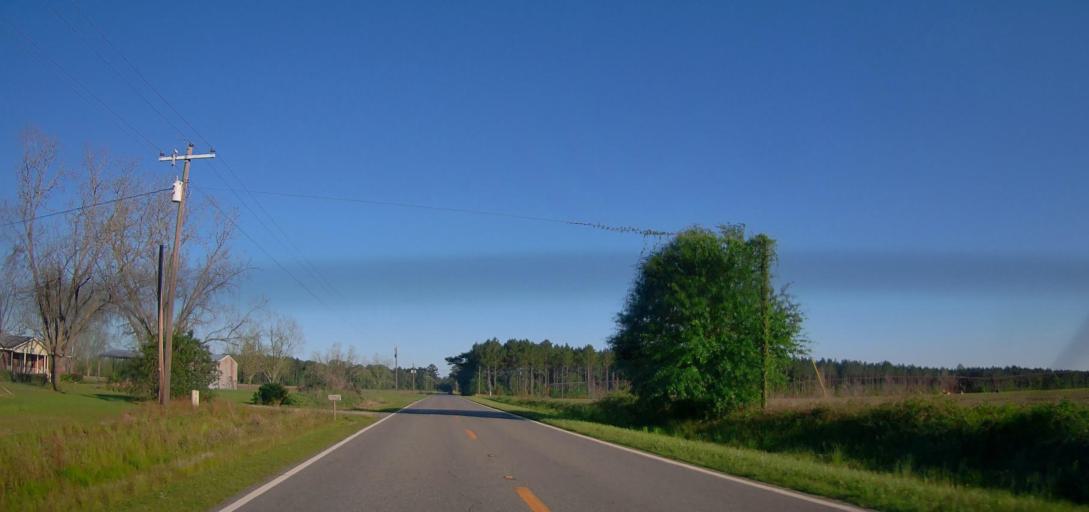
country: US
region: Georgia
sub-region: Ben Hill County
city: Fitzgerald
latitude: 31.6640
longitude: -83.1819
